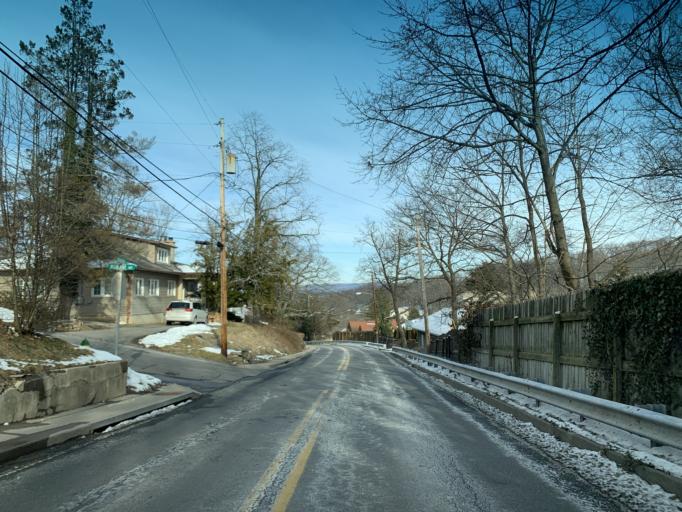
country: US
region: Maryland
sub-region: Allegany County
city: La Vale
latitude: 39.6476
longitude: -78.7887
